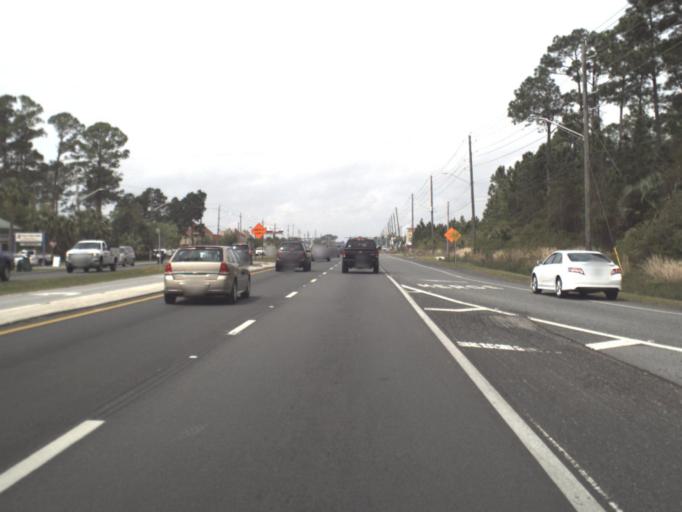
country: US
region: Florida
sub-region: Santa Rosa County
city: Navarre
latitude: 30.4017
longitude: -86.8745
